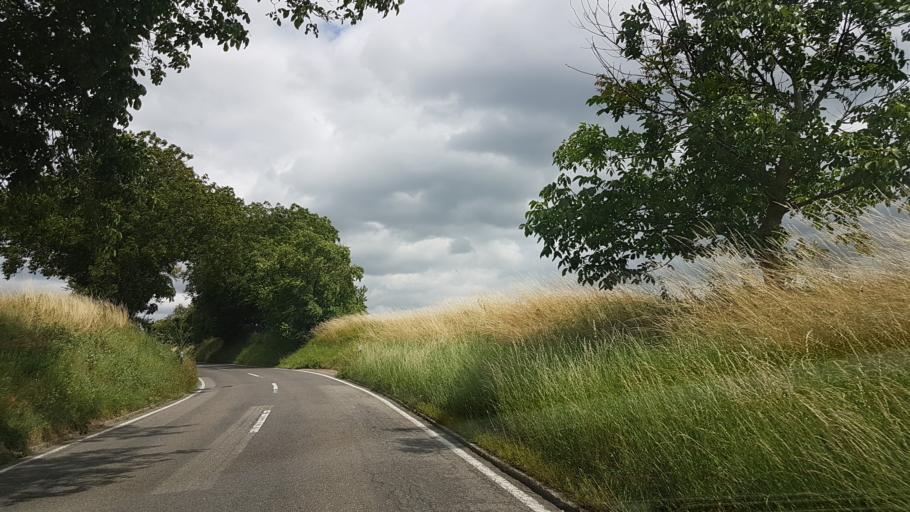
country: DE
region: Baden-Wuerttemberg
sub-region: Regierungsbezirk Stuttgart
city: Ittlingen
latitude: 49.2430
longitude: 8.9310
